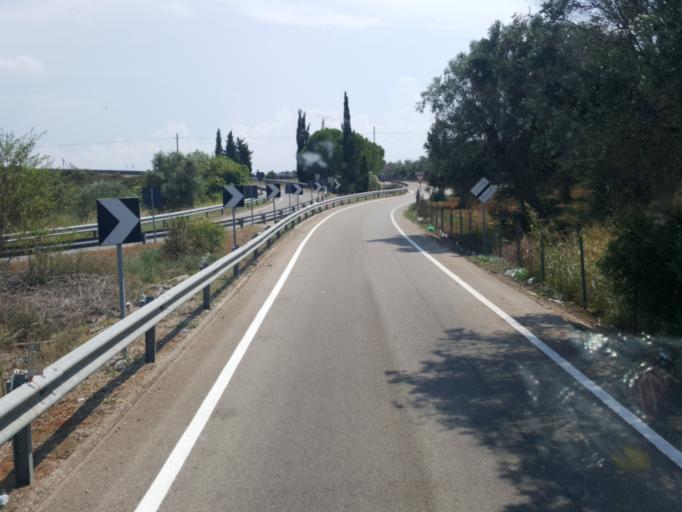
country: IT
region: Apulia
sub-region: Provincia di Lecce
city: Trepuzzi
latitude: 40.4407
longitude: 18.0771
